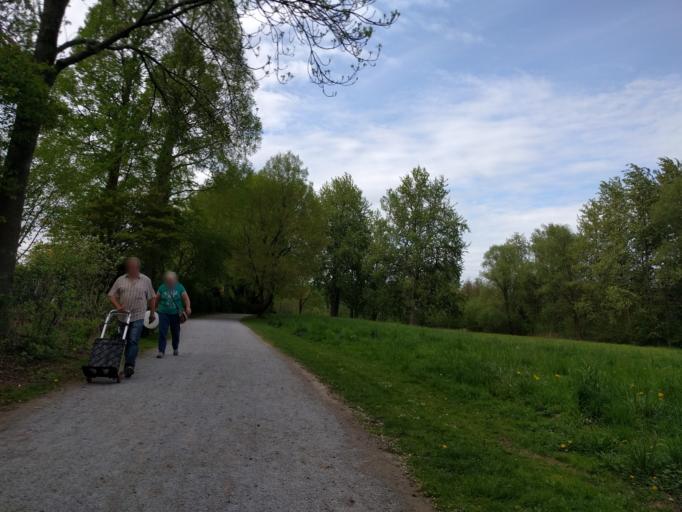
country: DE
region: North Rhine-Westphalia
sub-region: Regierungsbezirk Detmold
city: Bielefeld
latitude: 52.0517
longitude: 8.5324
